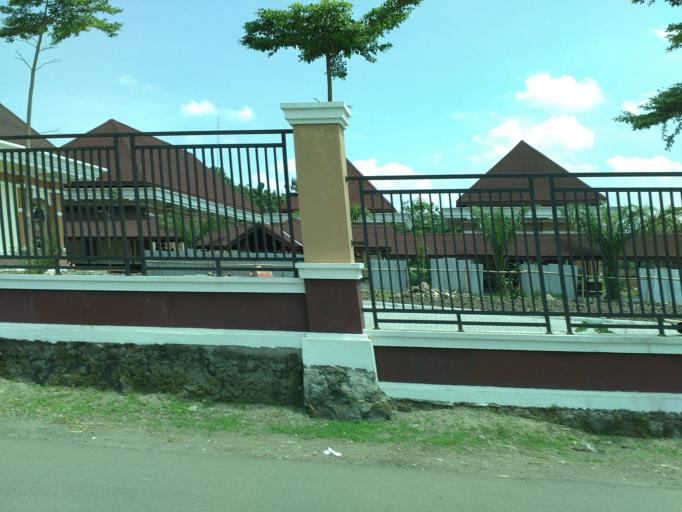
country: ID
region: Central Java
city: Klaten
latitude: -7.7043
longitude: 110.5966
